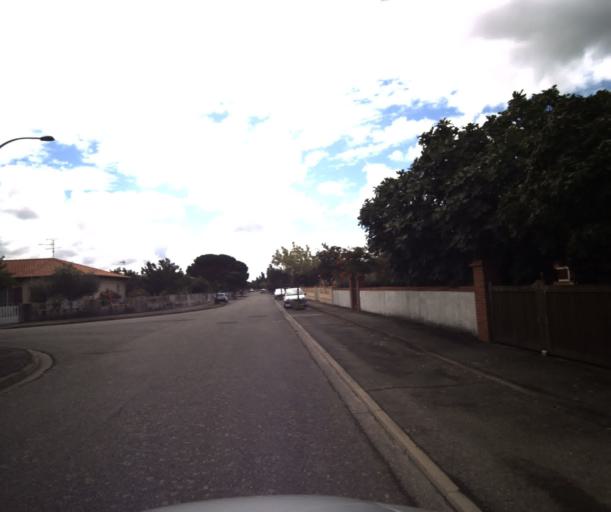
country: FR
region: Midi-Pyrenees
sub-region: Departement de la Haute-Garonne
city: Pinsaguel
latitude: 43.5178
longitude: 1.3894
